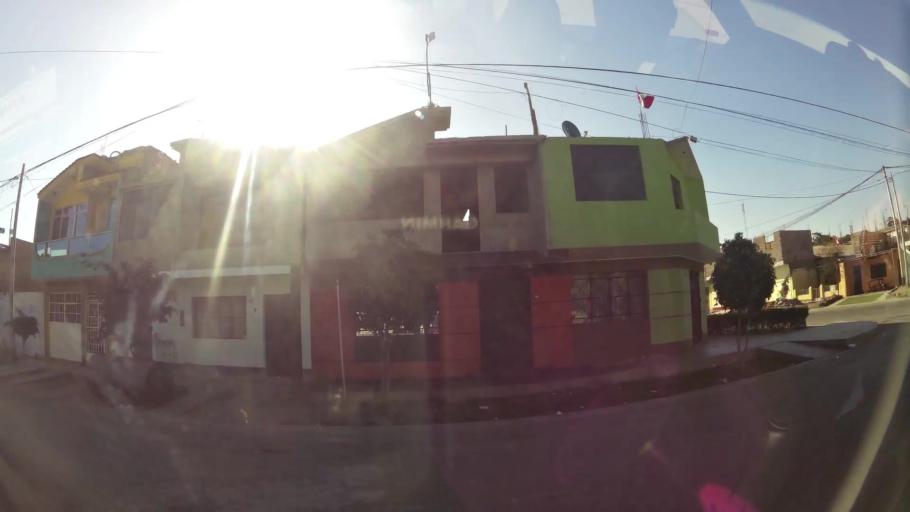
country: PE
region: Ica
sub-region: Provincia de Ica
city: La Tinguina
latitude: -14.0444
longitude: -75.7044
